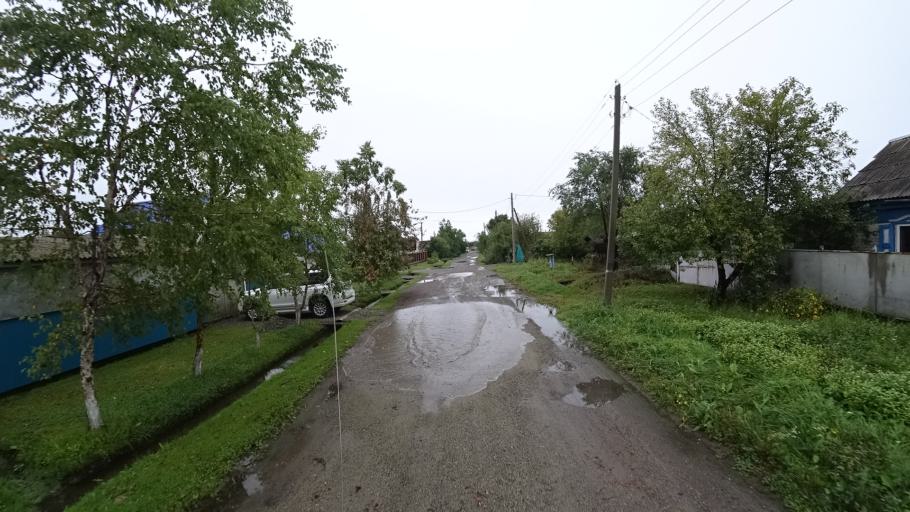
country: RU
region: Primorskiy
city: Monastyrishche
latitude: 44.2085
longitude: 132.4517
